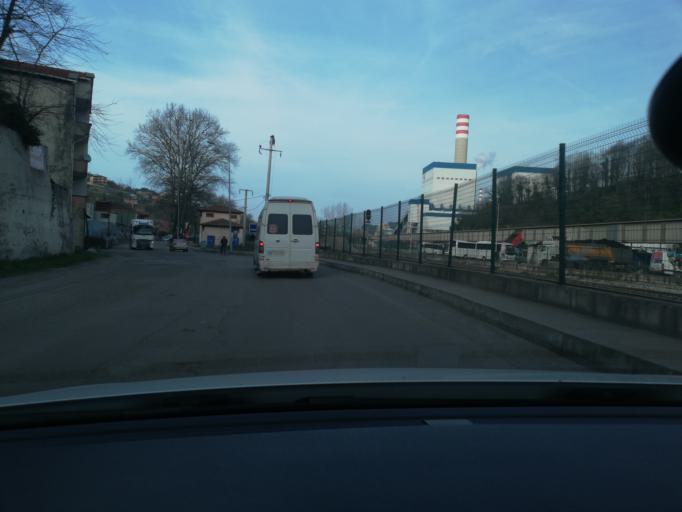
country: TR
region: Zonguldak
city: Kilimli
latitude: 41.5006
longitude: 31.8803
